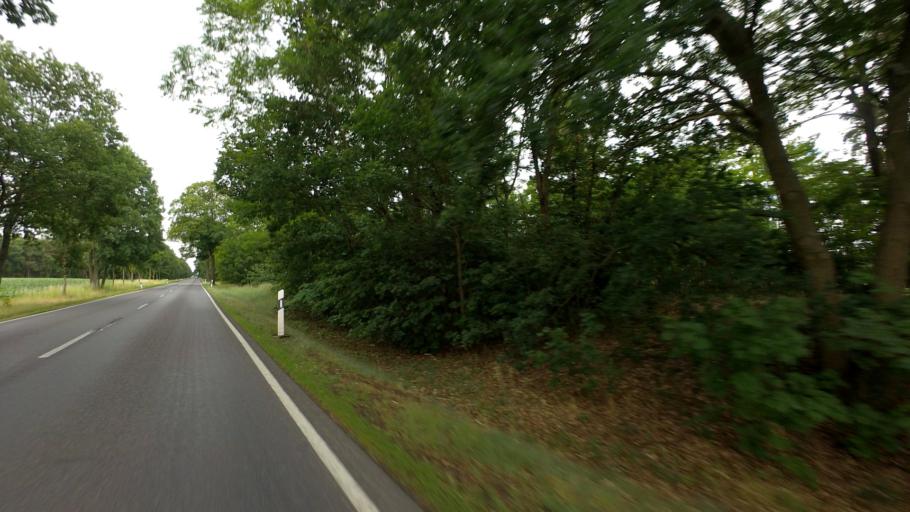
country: DE
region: Brandenburg
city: Crinitz
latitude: 51.8053
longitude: 13.8257
